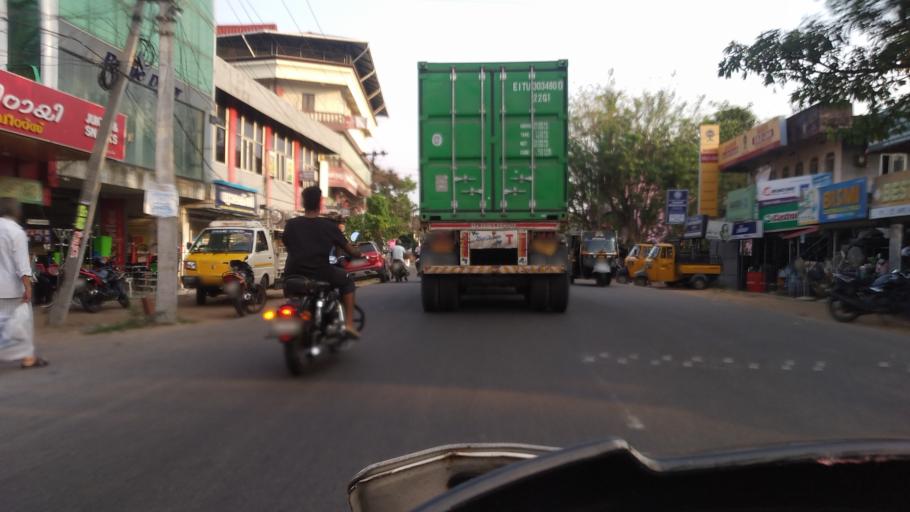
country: IN
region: Kerala
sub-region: Thrissur District
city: Irinjalakuda
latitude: 10.3193
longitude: 76.1457
